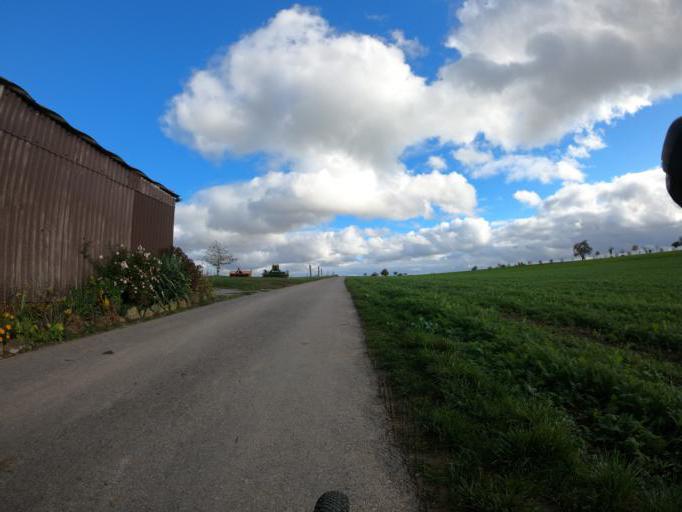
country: DE
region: Baden-Wuerttemberg
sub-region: Regierungsbezirk Stuttgart
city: Magstadt
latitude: 48.7200
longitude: 8.9268
